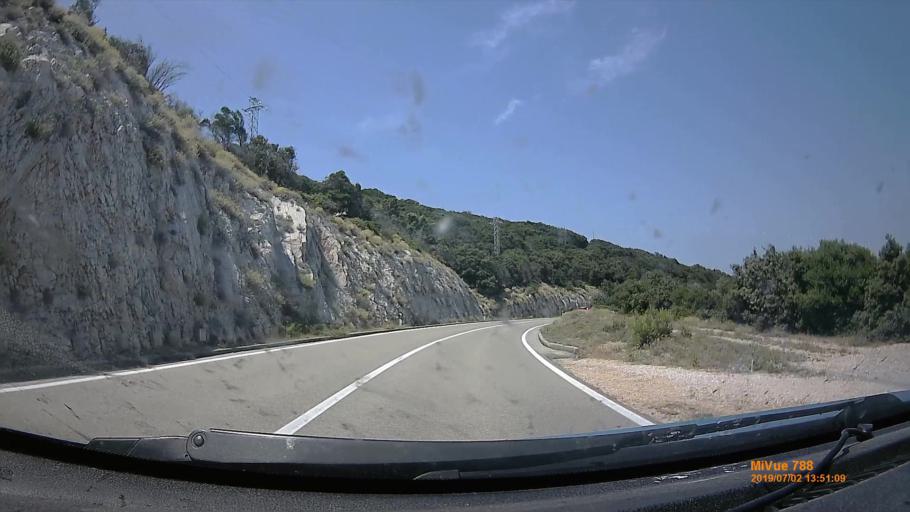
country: HR
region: Primorsko-Goranska
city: Mali Losinj
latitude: 44.6022
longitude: 14.4047
